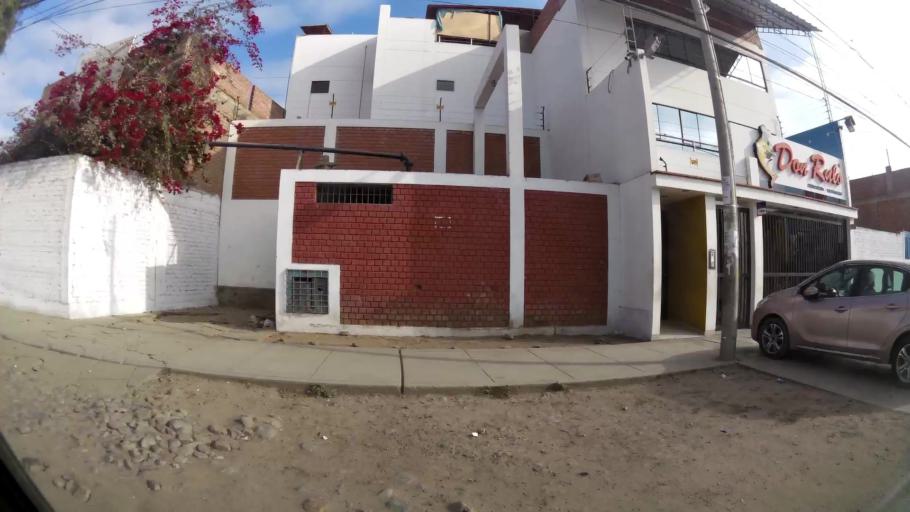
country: PE
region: La Libertad
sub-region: Provincia de Trujillo
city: La Esperanza
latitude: -8.0911
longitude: -79.0467
